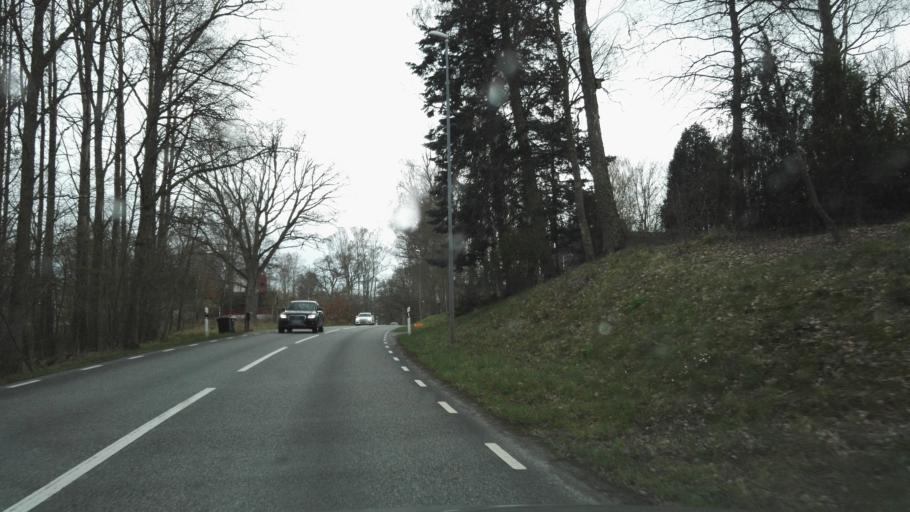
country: SE
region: Skane
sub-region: Hassleholms Kommun
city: Hastveda
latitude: 56.1931
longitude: 13.8988
